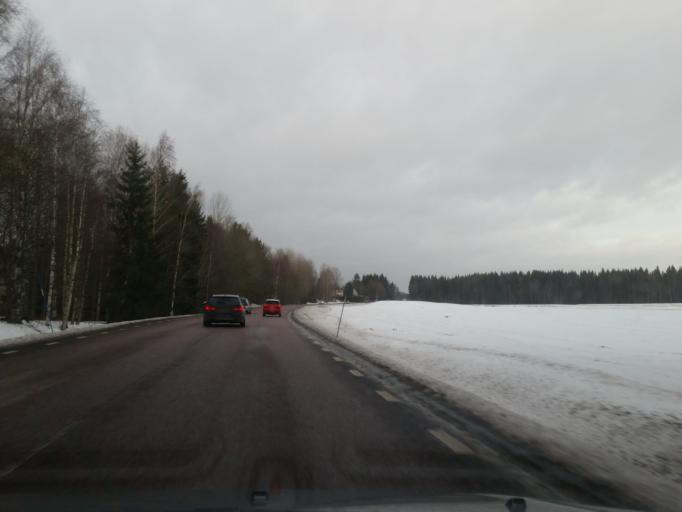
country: SE
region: Gaevleborg
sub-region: Sandvikens Kommun
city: Sandviken
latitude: 60.6643
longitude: 16.6953
